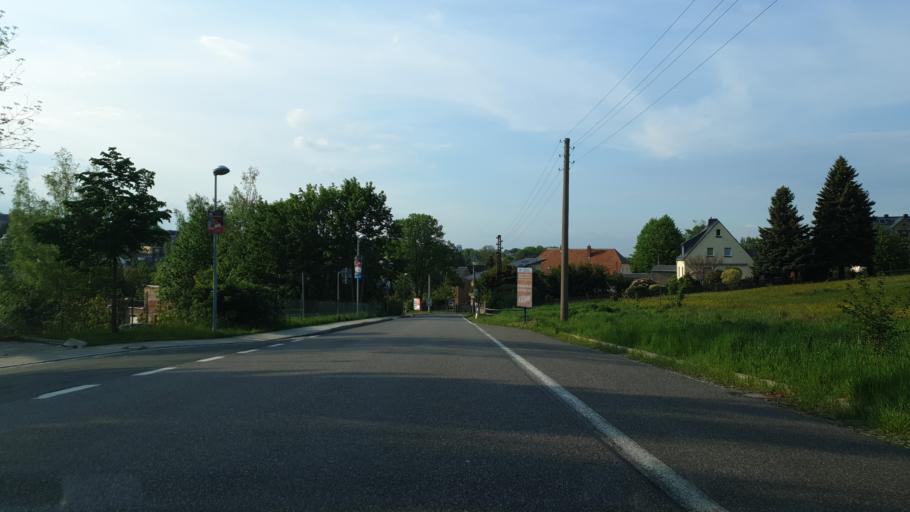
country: DE
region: Saxony
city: Stollberg
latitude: 50.7083
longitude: 12.7843
